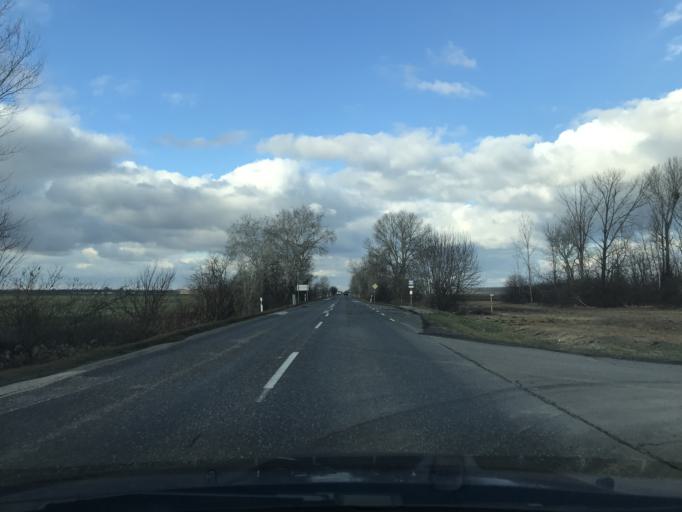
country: HU
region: Bacs-Kiskun
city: Dusnok
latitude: 46.3378
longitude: 18.9799
